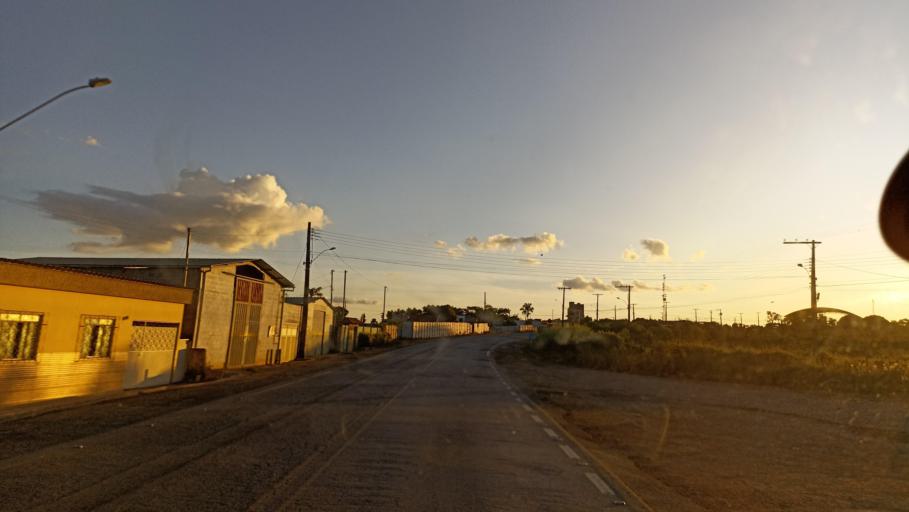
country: BR
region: Minas Gerais
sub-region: Sao Joao Del Rei
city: Sao Joao del Rei
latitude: -21.2427
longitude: -44.4035
